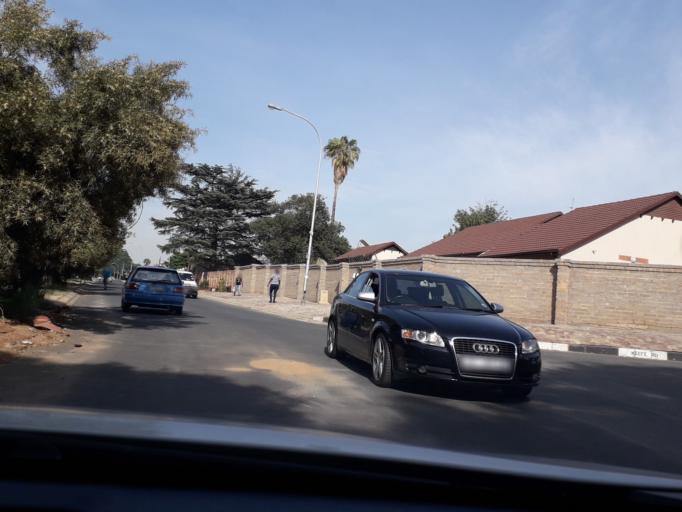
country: ZA
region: Gauteng
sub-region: City of Johannesburg Metropolitan Municipality
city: Modderfontein
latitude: -26.1183
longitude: 28.1063
